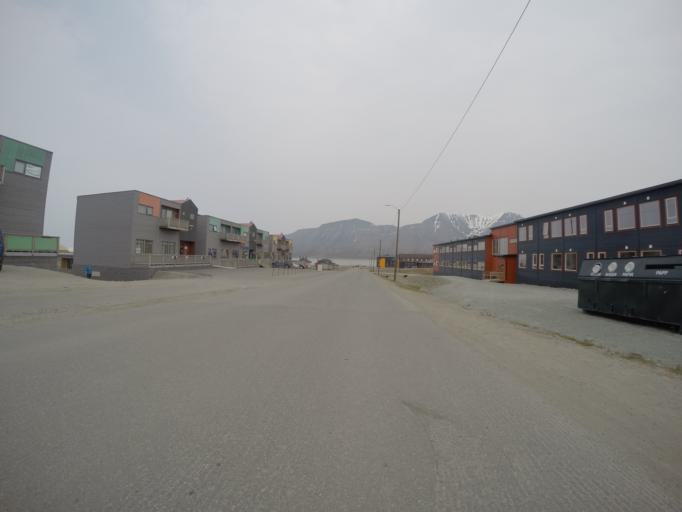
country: SJ
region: Svalbard
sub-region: Spitsbergen
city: Longyearbyen
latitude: 78.2212
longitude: 15.6430
